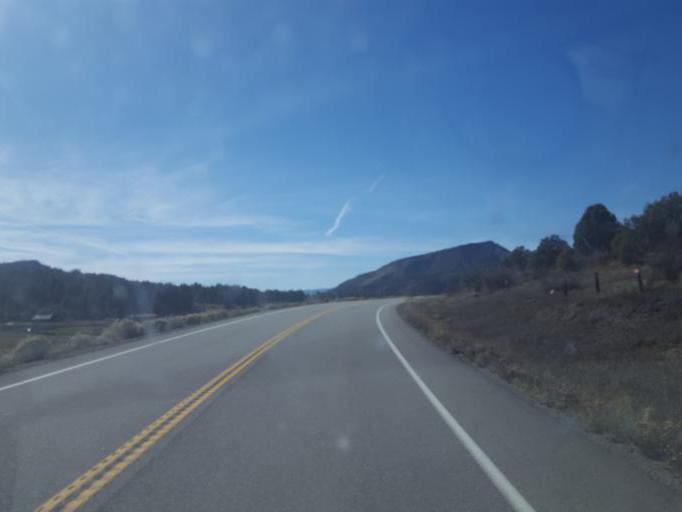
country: US
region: Colorado
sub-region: Archuleta County
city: Pagosa Springs
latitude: 37.2293
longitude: -107.1924
